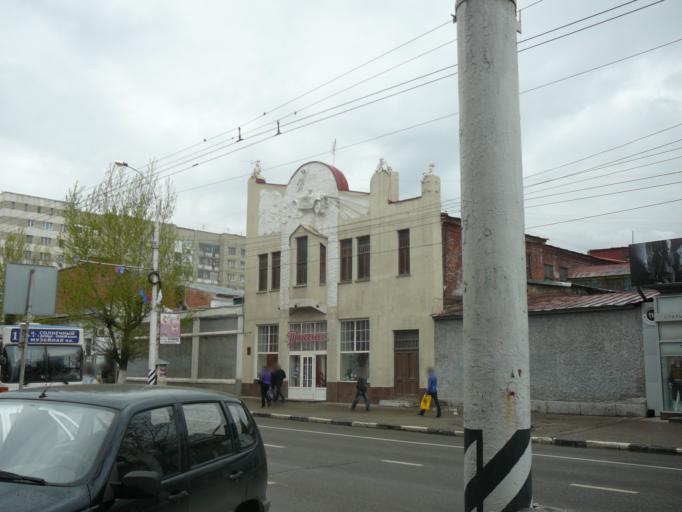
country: RU
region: Saratov
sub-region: Saratovskiy Rayon
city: Saratov
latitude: 51.5361
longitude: 46.0247
